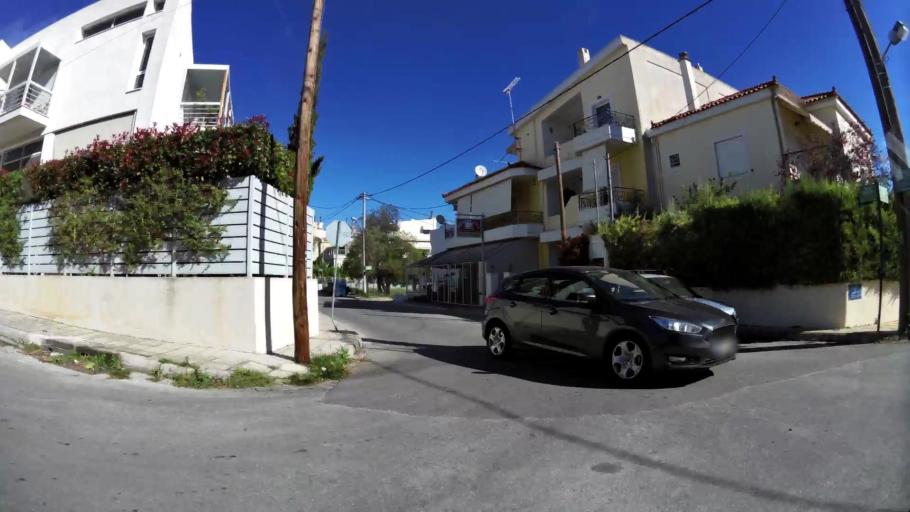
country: GR
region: Attica
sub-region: Nomarchia Anatolikis Attikis
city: Gerakas
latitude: 38.0074
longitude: 23.8515
